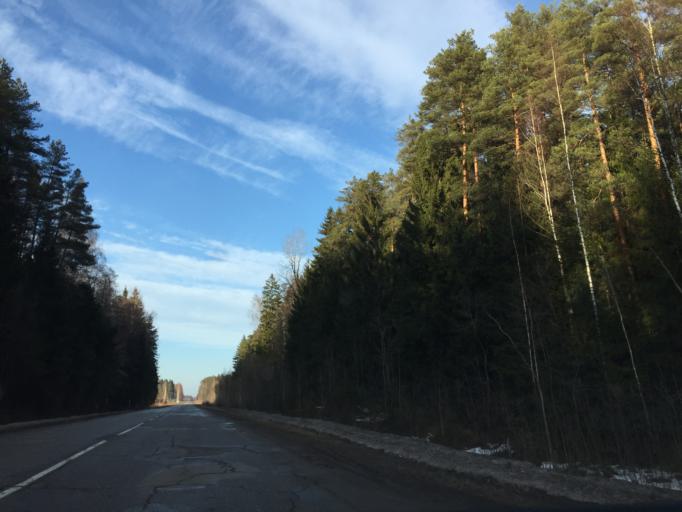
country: LV
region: Lecava
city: Iecava
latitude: 56.7120
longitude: 24.1125
